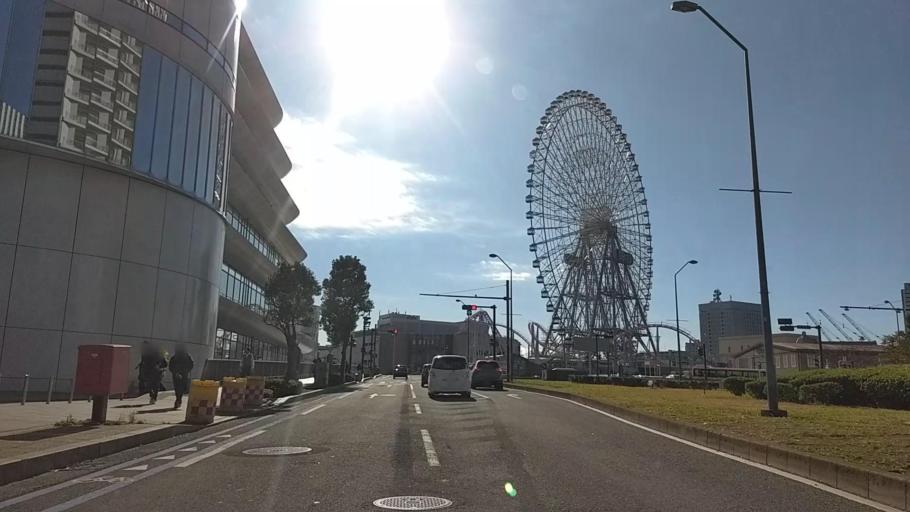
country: JP
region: Kanagawa
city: Yokohama
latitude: 35.4575
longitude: 139.6359
